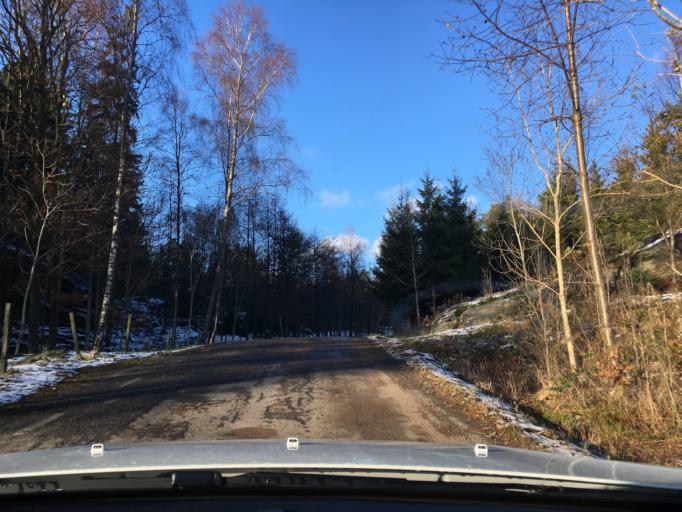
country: SE
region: Vaestra Goetaland
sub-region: Tjorns Kommun
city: Myggenas
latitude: 58.0902
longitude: 11.7498
